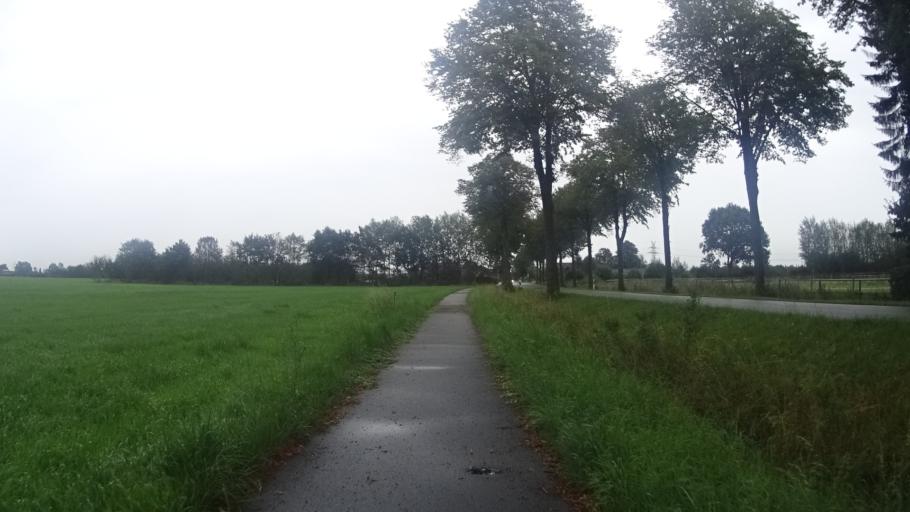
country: DE
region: Schleswig-Holstein
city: Seeth-Ekholt
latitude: 53.7571
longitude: 9.7359
